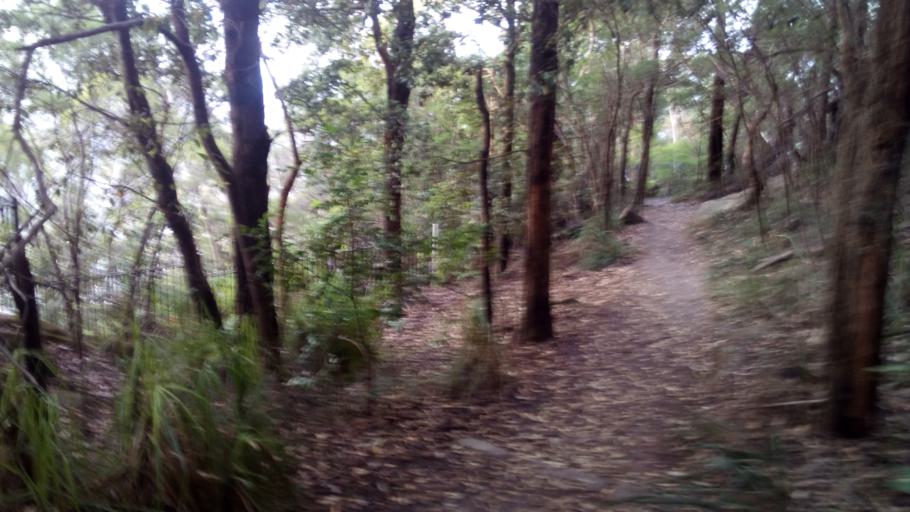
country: AU
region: New South Wales
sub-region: Wollongong
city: Mount Keira
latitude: -34.4034
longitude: 150.8565
